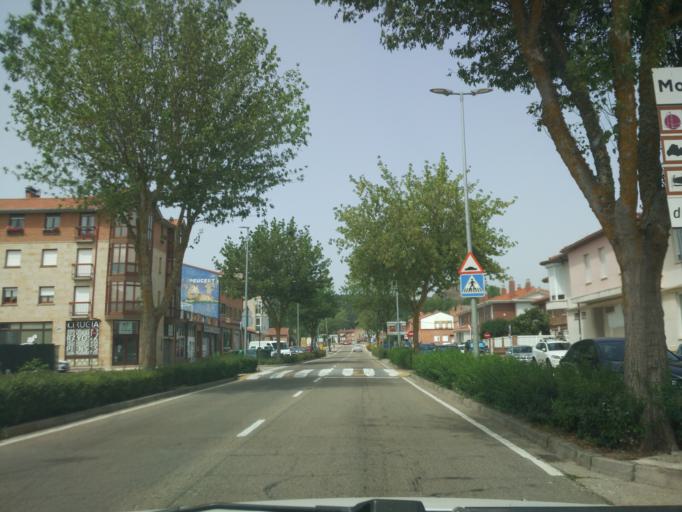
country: ES
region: Castille and Leon
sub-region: Provincia de Palencia
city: Aguilar de Campoo
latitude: 42.7897
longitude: -4.2661
